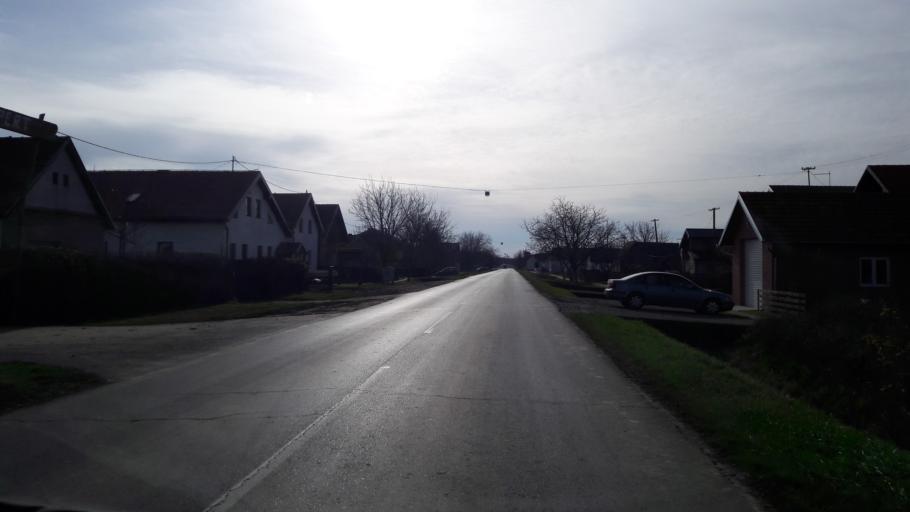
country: HR
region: Osjecko-Baranjska
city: Semeljci
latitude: 45.3134
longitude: 18.5573
